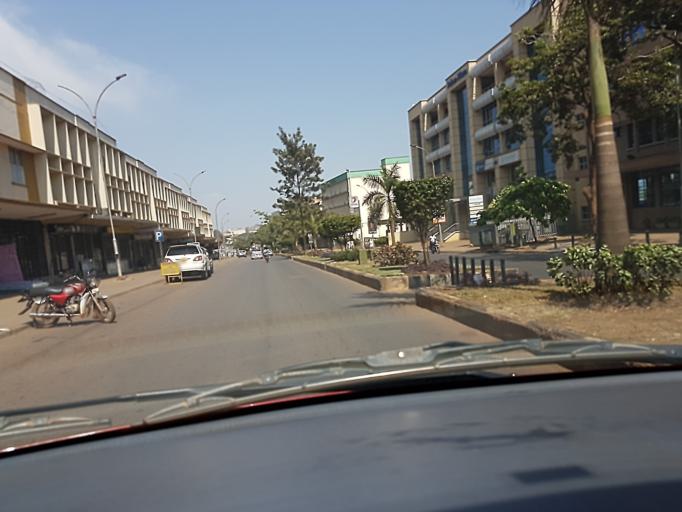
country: UG
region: Central Region
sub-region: Kampala District
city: Kampala
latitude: 0.3143
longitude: 32.5898
